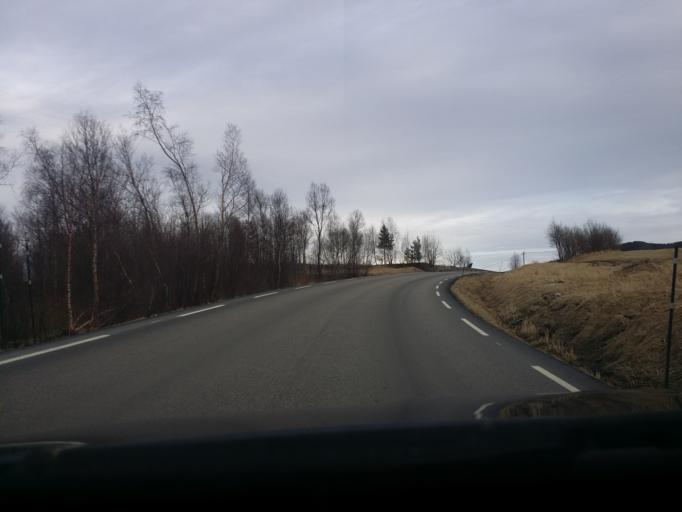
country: NO
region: More og Romsdal
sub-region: Halsa
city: Liaboen
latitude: 63.1359
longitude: 8.4490
